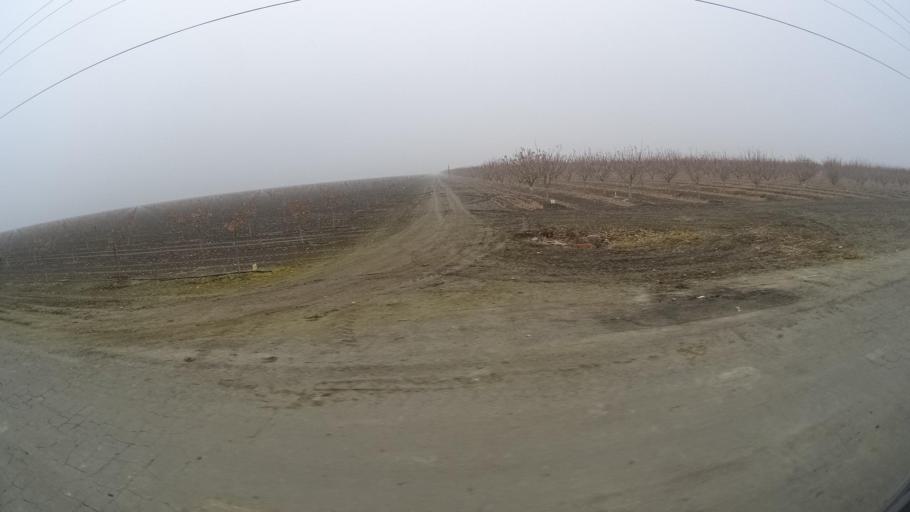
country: US
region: California
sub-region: Kern County
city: Buttonwillow
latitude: 35.4482
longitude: -119.5177
